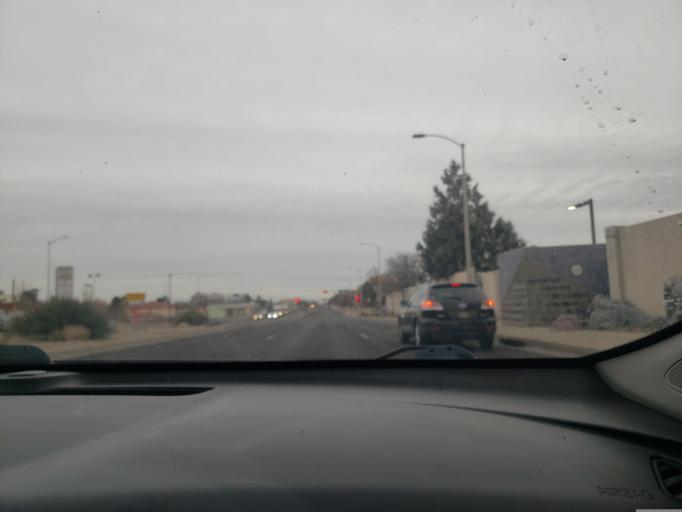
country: US
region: New Mexico
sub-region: Bernalillo County
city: Albuquerque
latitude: 35.0935
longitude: -106.5862
